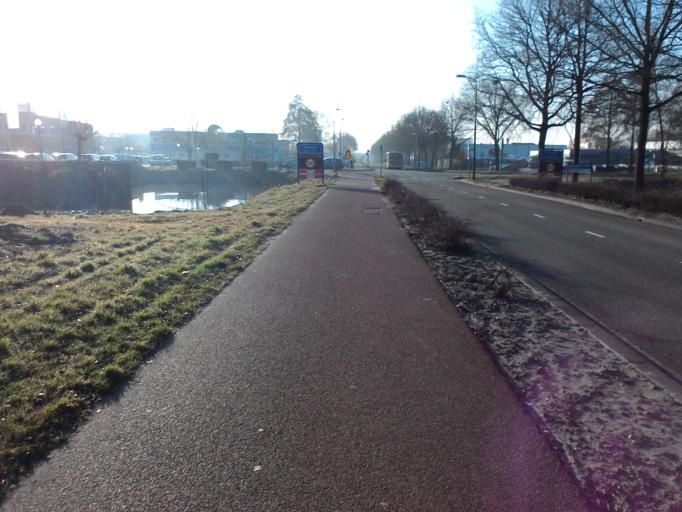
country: NL
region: Utrecht
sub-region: Stichtse Vecht
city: Maarssen
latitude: 52.1260
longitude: 5.0408
